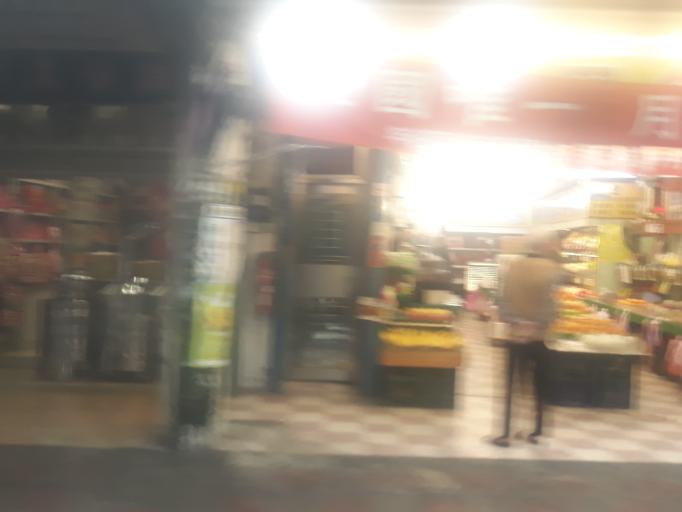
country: TW
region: Taipei
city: Taipei
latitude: 24.9876
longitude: 121.5696
